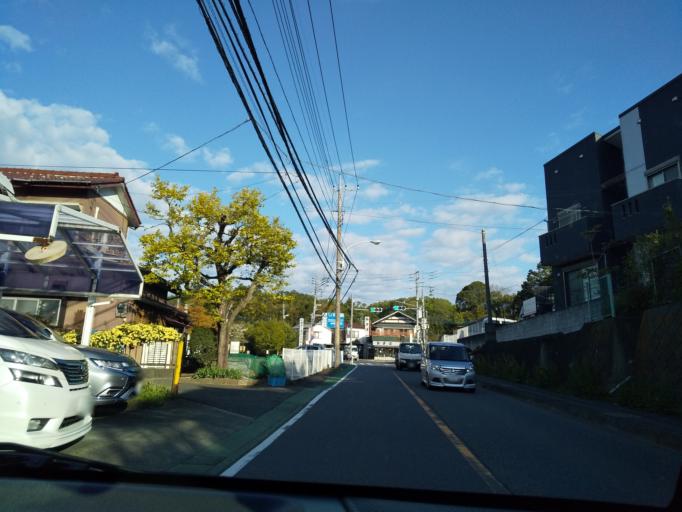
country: JP
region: Tokyo
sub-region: Machida-shi
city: Machida
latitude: 35.5949
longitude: 139.4542
